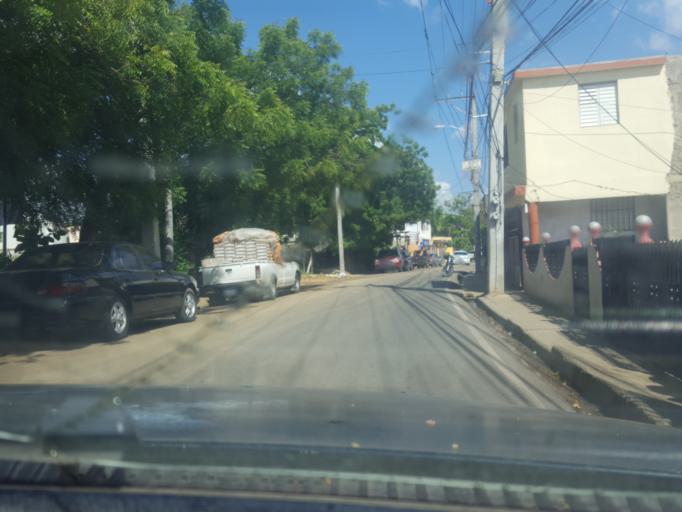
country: DO
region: Santiago
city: Santiago de los Caballeros
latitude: 19.4872
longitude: -70.7021
